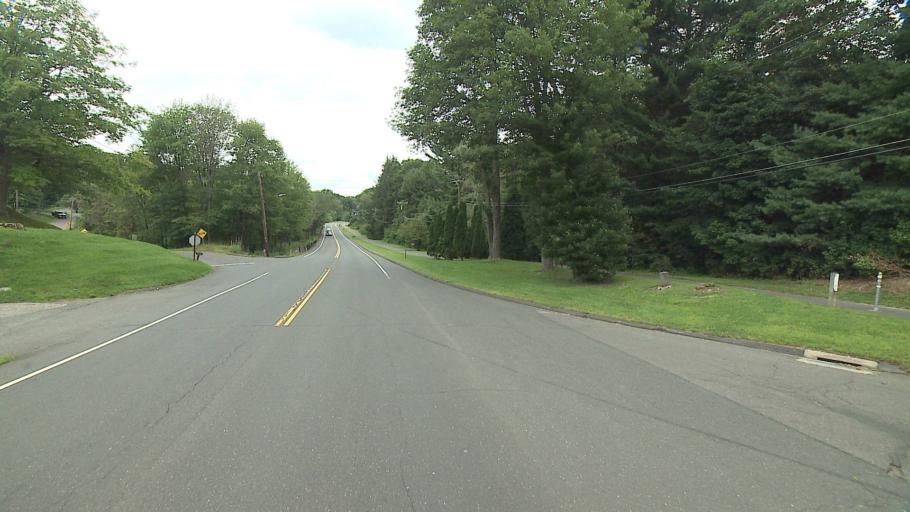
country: US
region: Connecticut
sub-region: New Haven County
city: Middlebury
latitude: 41.5335
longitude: -73.1239
